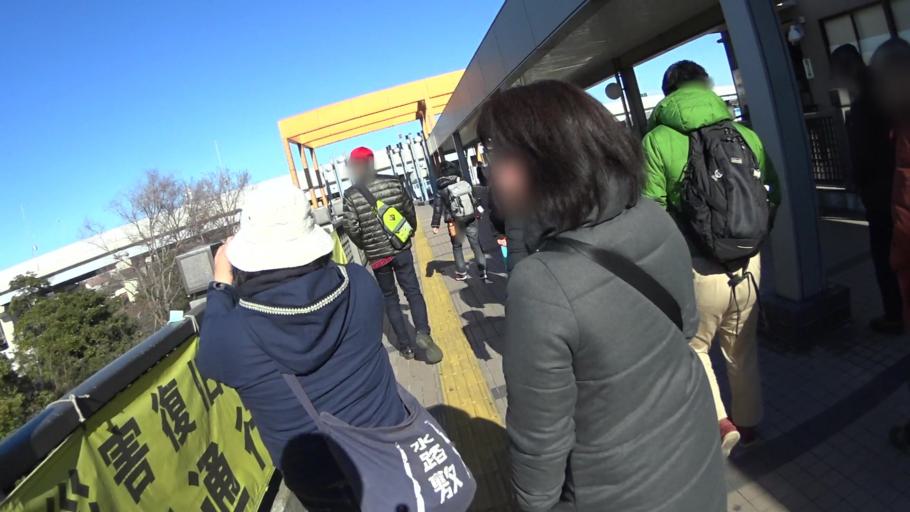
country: JP
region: Tokyo
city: Urayasu
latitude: 35.6383
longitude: 139.8836
